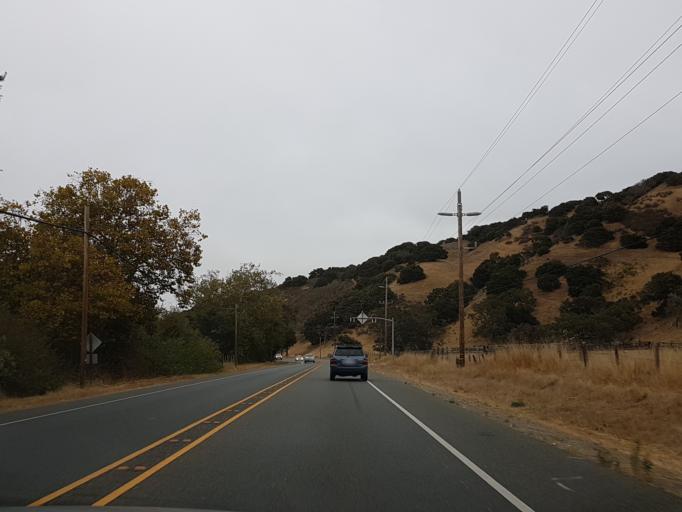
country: US
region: California
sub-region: Monterey County
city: Carmel Valley Village
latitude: 36.5826
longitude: -121.7156
